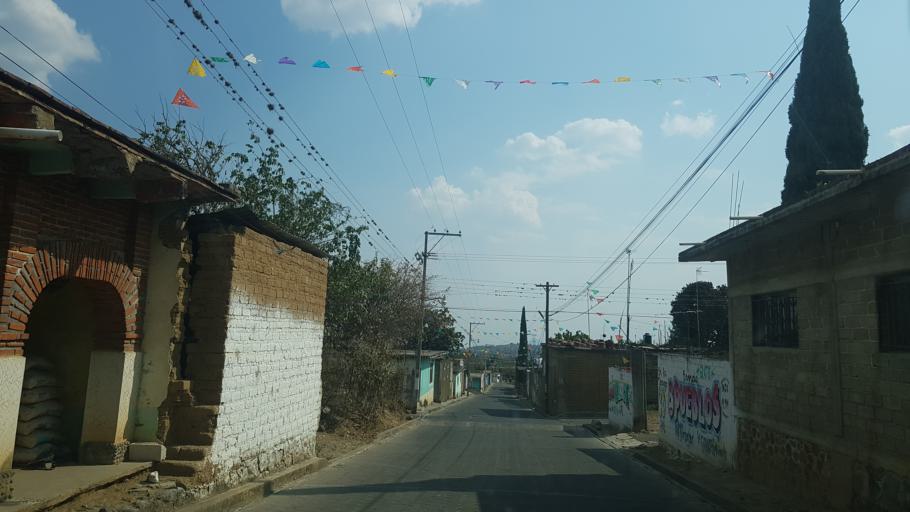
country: MX
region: Puebla
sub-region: Tochimilco
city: San Antonio Alpanocan
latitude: 18.8352
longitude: -98.7025
